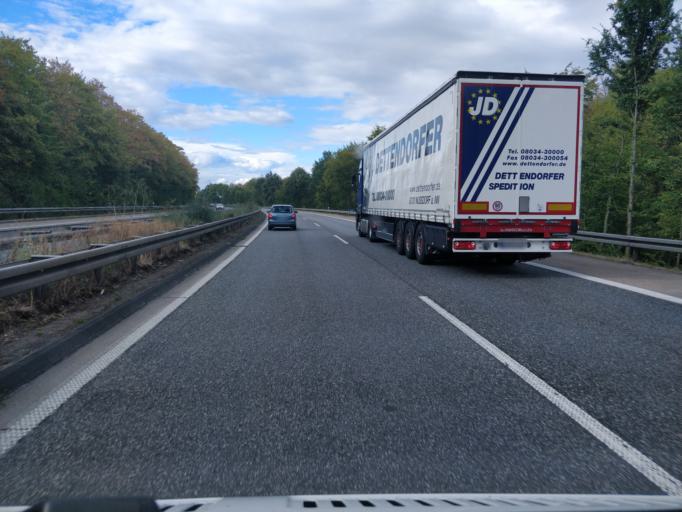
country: DE
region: North Rhine-Westphalia
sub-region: Regierungsbezirk Koln
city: Wachtberg
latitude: 50.6730
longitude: 7.0625
